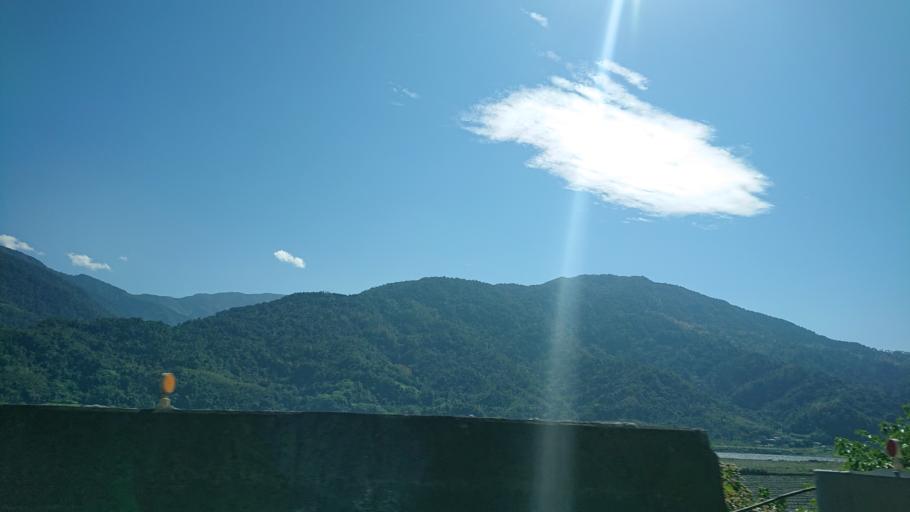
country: TW
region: Taiwan
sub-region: Yilan
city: Yilan
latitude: 24.6036
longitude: 121.5189
